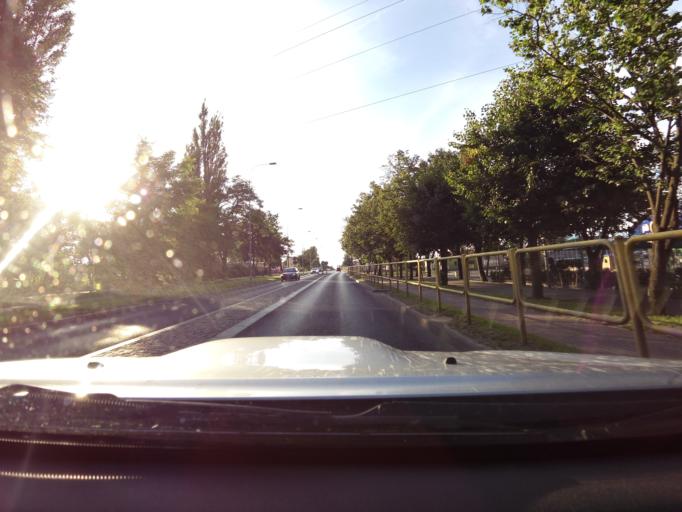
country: PL
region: Warmian-Masurian Voivodeship
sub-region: Powiat ostrodzki
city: Ostroda
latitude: 53.6902
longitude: 19.9826
